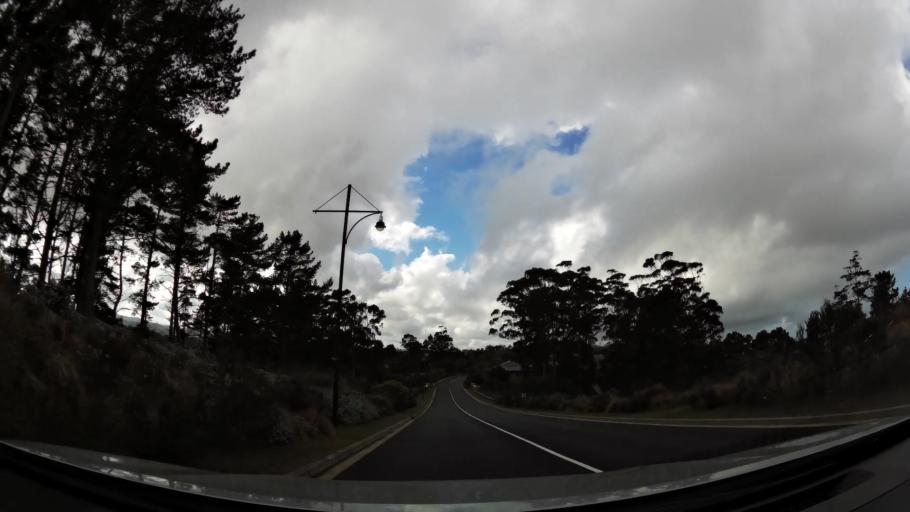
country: ZA
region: Western Cape
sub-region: Eden District Municipality
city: Knysna
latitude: -34.0658
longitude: 23.1019
